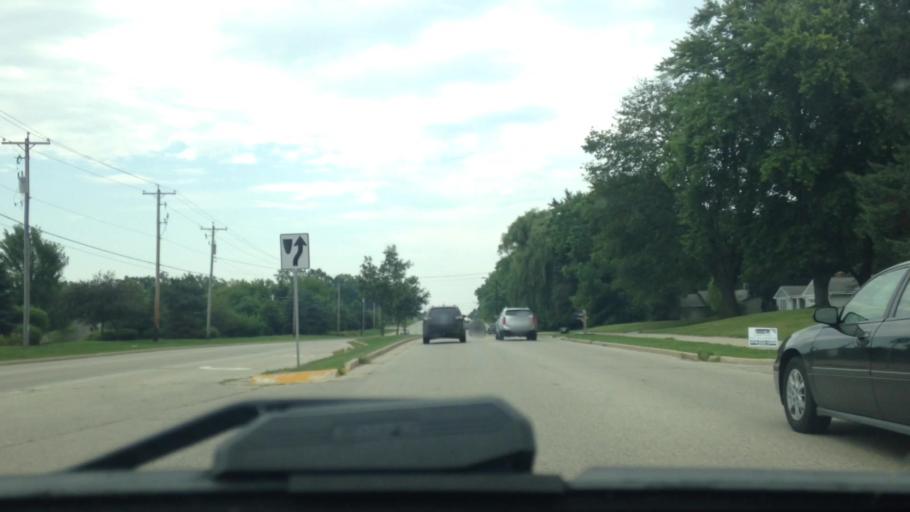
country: US
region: Wisconsin
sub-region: Waukesha County
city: Menomonee Falls
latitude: 43.1443
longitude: -88.1046
